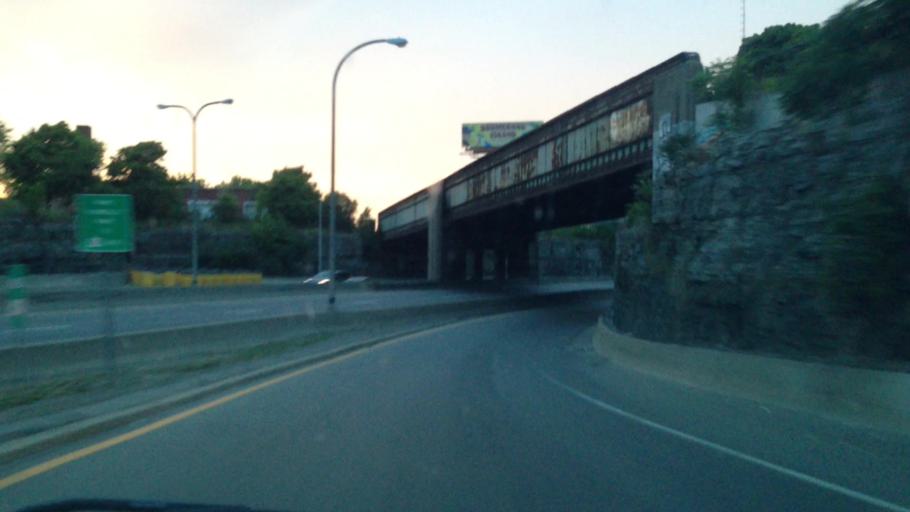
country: US
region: New York
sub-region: Erie County
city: Buffalo
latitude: 42.9228
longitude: -78.8428
